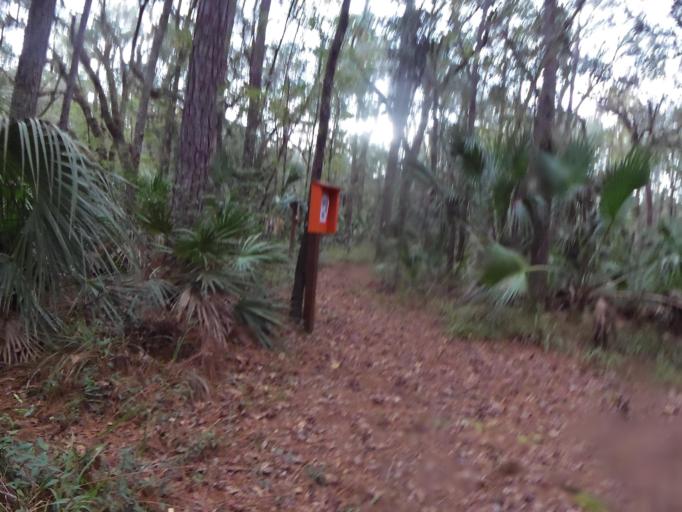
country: US
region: Florida
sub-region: Putnam County
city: Palatka
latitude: 29.6740
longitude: -81.7562
